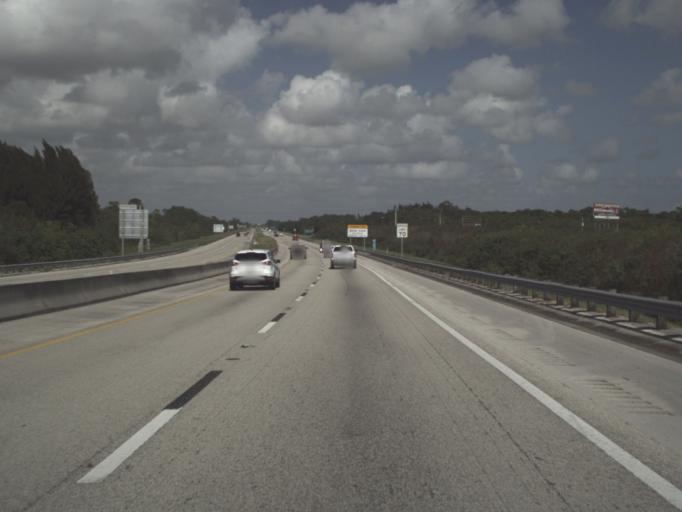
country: US
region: Florida
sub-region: Saint Lucie County
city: Fort Pierce South
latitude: 27.4150
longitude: -80.4033
